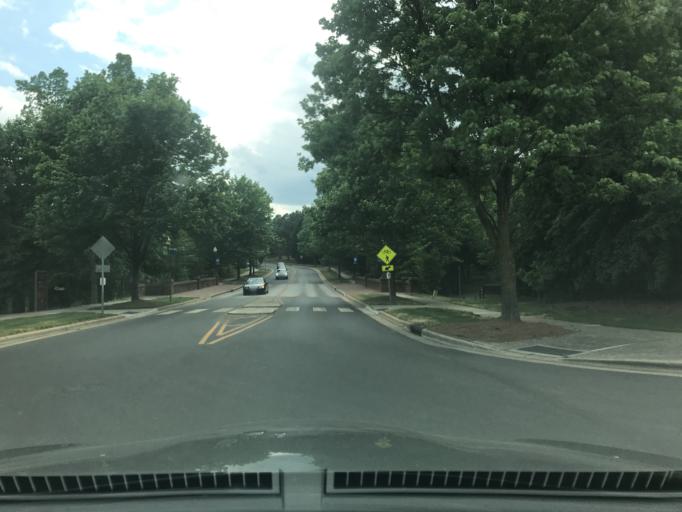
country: US
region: North Carolina
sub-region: Wake County
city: Wake Forest
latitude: 35.9128
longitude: -78.5855
